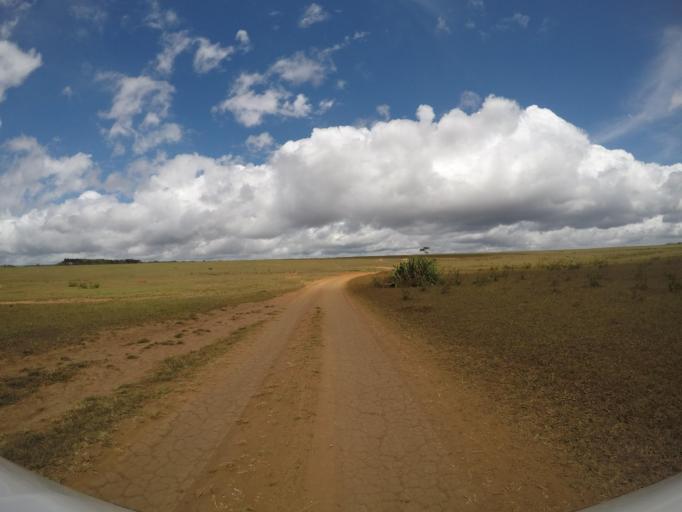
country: TL
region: Lautem
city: Lospalos
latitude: -8.4583
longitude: 126.9843
